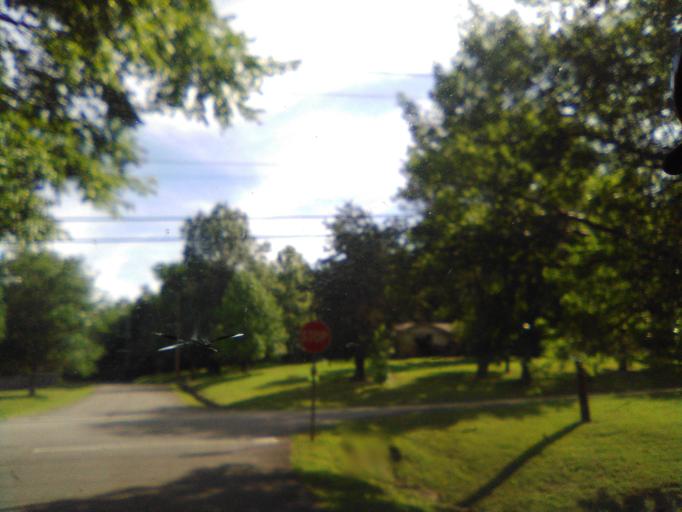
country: US
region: Tennessee
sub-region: Davidson County
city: Belle Meade
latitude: 36.1133
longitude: -86.9024
